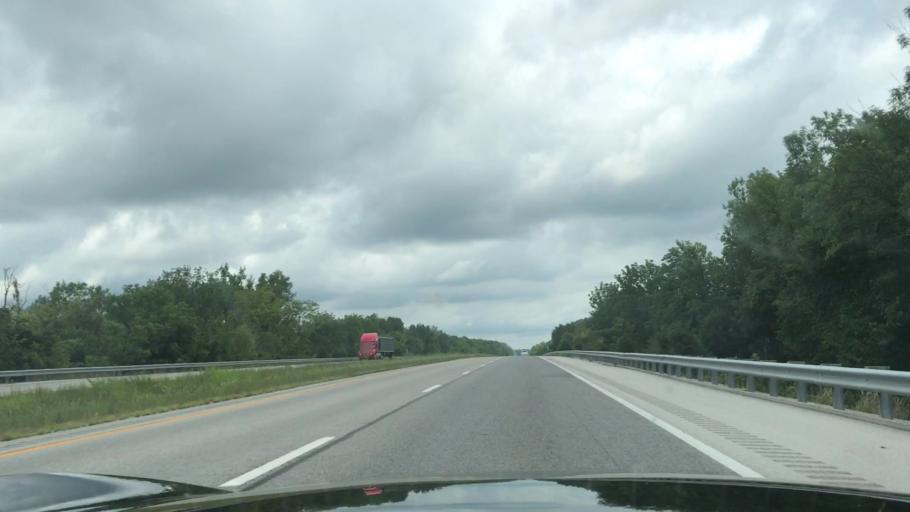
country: US
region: Kentucky
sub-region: Butler County
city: Morgantown
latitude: 37.1343
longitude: -86.6484
